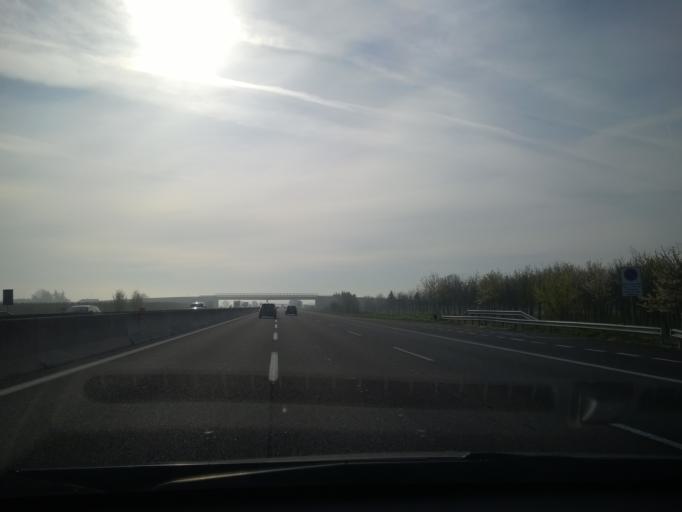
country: IT
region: Emilia-Romagna
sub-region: Provincia di Bologna
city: Castel Guelfo di Bologna
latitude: 44.4069
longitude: 11.6735
